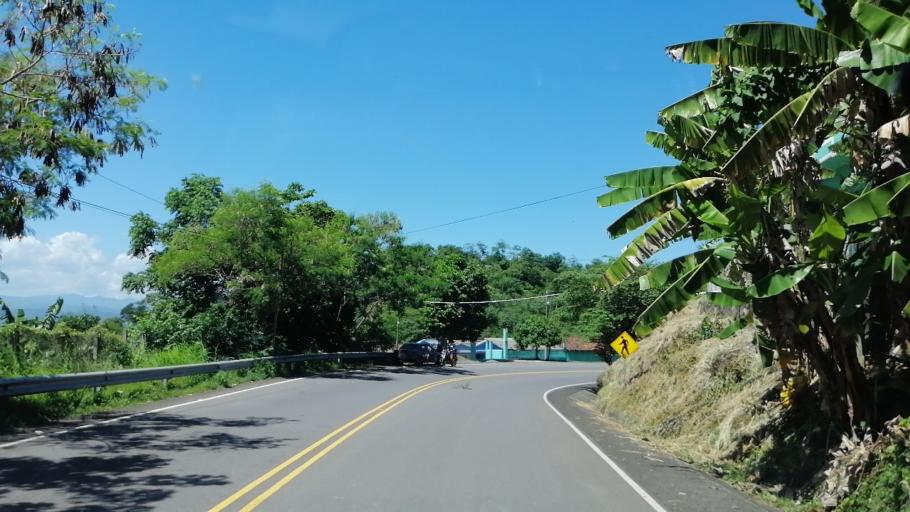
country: SV
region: San Miguel
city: Ciudad Barrios
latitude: 13.8135
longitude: -88.1794
